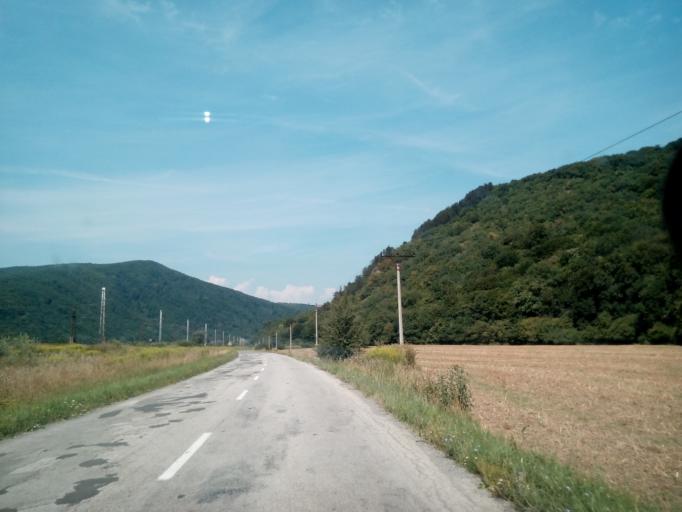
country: SK
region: Kosicky
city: Kosice
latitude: 48.8212
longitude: 21.2333
